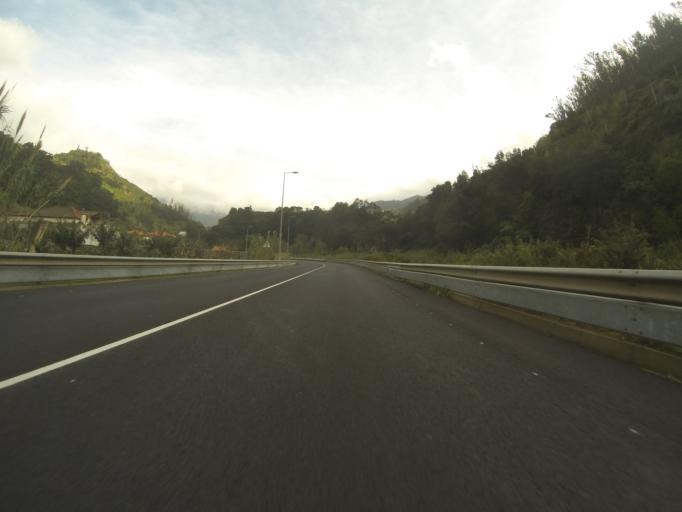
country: PT
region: Madeira
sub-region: Sao Vicente
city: Sao Vicente
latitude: 32.7989
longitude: -17.0425
